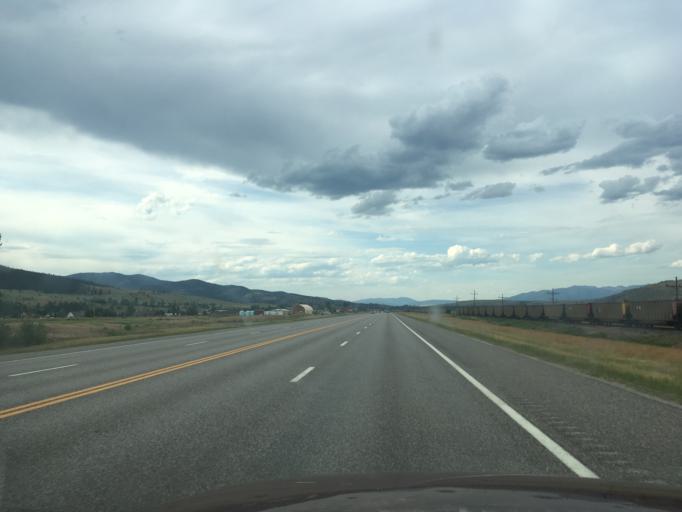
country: US
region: Montana
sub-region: Missoula County
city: Lolo
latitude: 46.7060
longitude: -114.0750
